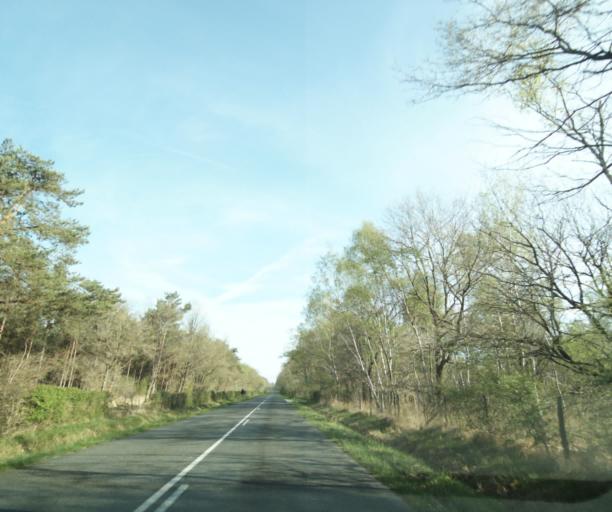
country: FR
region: Ile-de-France
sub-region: Departement de Seine-et-Marne
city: Vernou-la-Celle-sur-Seine
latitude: 48.4205
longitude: 2.8487
